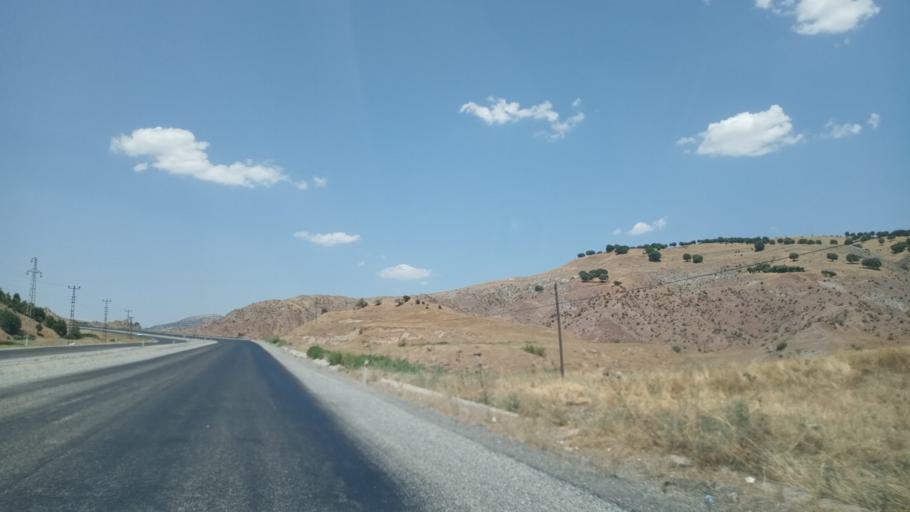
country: TR
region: Batman
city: Kozluk
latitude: 38.1715
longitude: 41.4519
